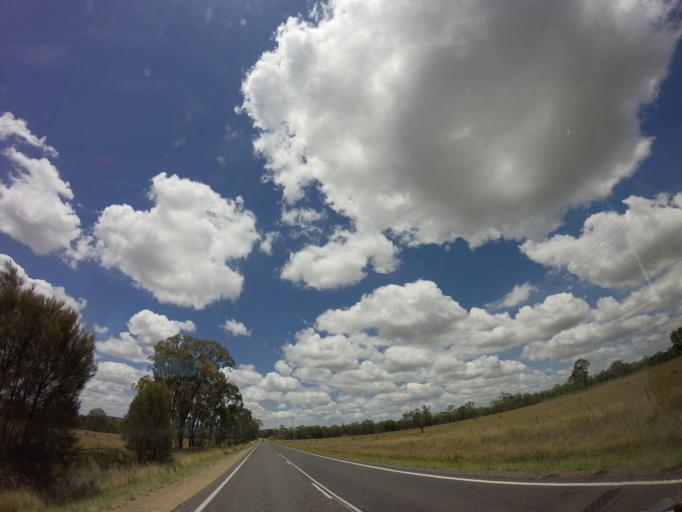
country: AU
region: Queensland
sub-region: Western Downs
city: Dalby
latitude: -27.9739
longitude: 151.1058
